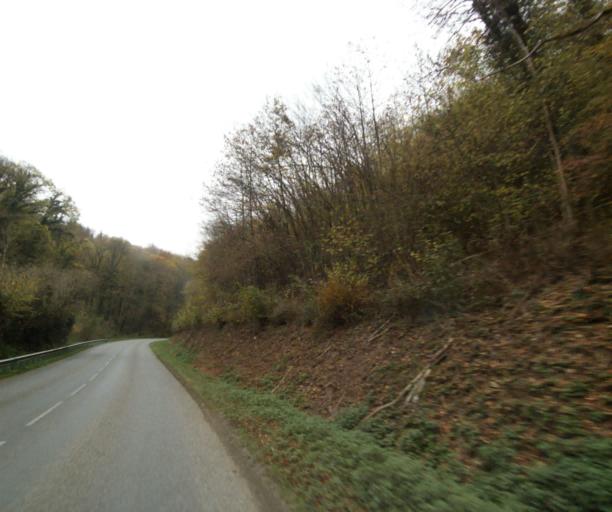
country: FR
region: Lorraine
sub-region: Departement de Meurthe-et-Moselle
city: Joeuf
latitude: 49.2468
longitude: 6.0191
